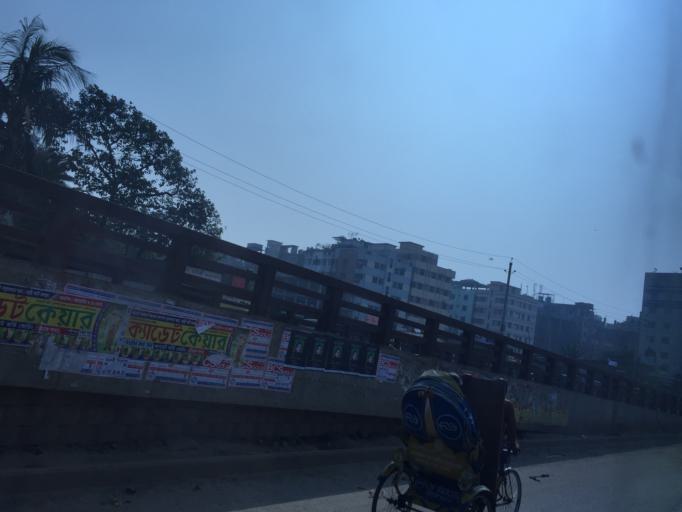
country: BD
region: Dhaka
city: Paltan
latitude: 23.7757
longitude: 90.4260
